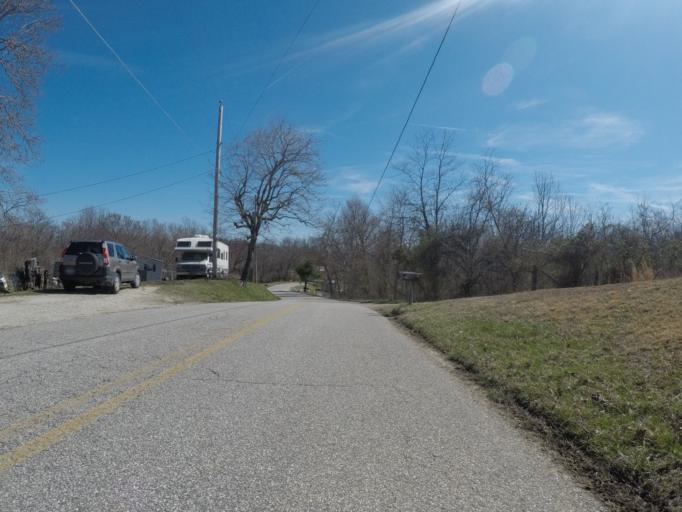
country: US
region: West Virginia
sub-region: Cabell County
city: Huntington
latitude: 38.4488
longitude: -82.4873
